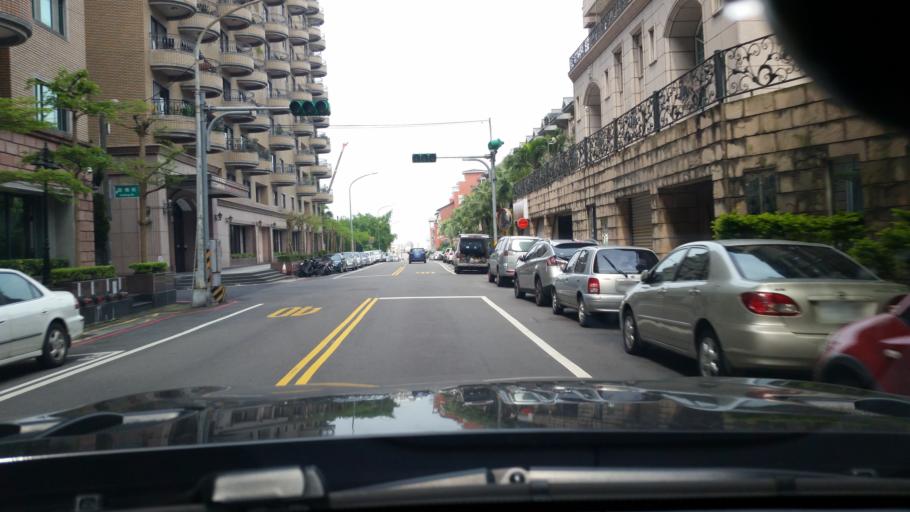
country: TW
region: Taiwan
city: Taoyuan City
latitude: 25.0615
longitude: 121.2967
